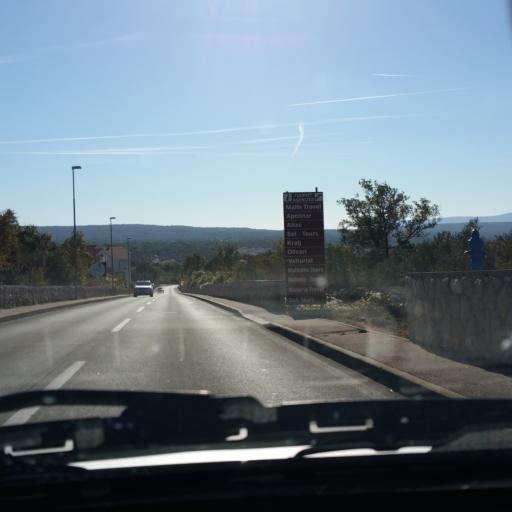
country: HR
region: Primorsko-Goranska
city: Njivice
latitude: 45.1298
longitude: 14.5399
